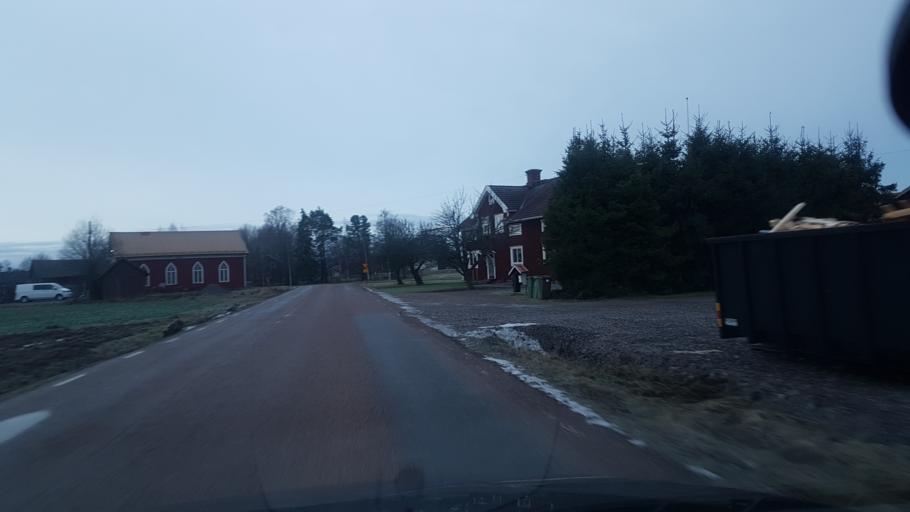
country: SE
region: Dalarna
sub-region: Saters Kommun
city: Saeter
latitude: 60.4249
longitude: 15.6566
